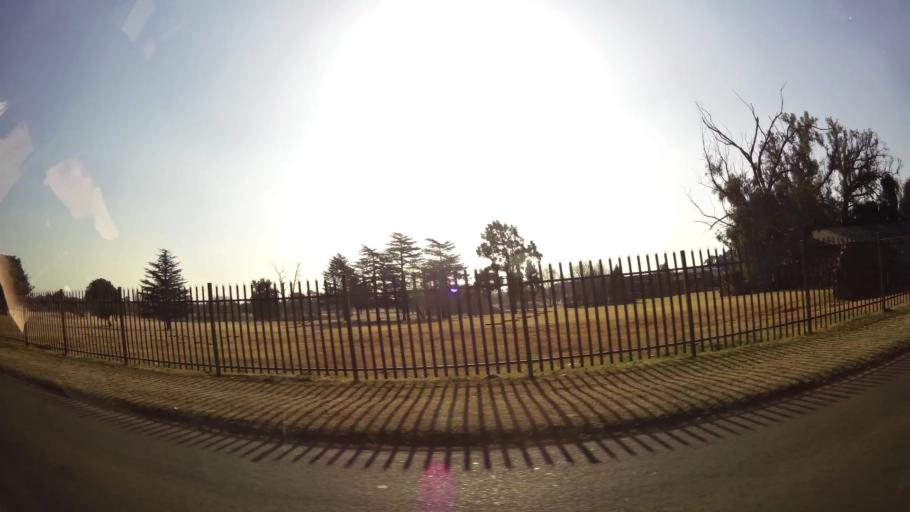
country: ZA
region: Gauteng
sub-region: West Rand District Municipality
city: Randfontein
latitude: -26.1577
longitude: 27.7143
